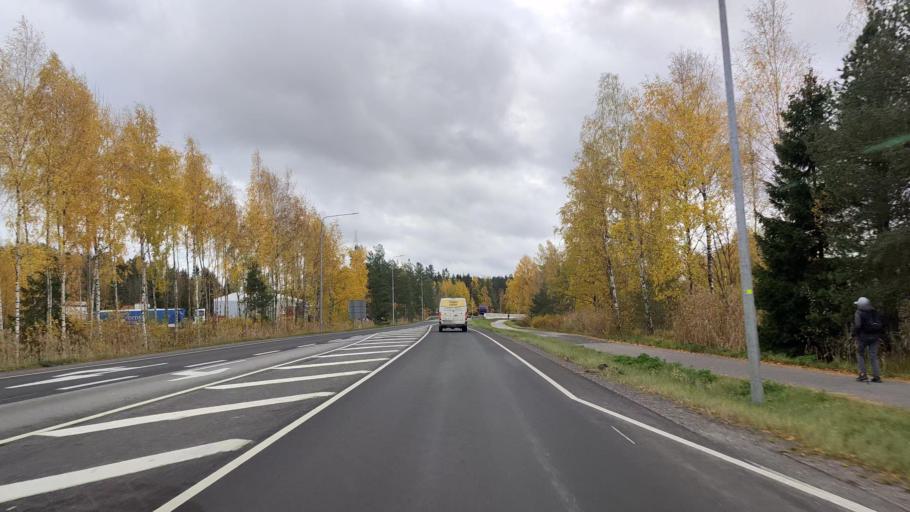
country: FI
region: Varsinais-Suomi
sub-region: Turku
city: Kaarina
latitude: 60.4326
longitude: 22.3845
